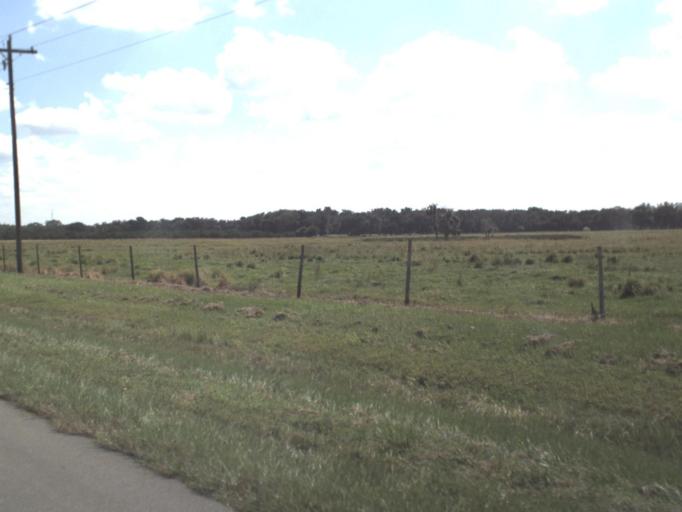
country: US
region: Florida
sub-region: Hardee County
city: Zolfo Springs
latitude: 27.4609
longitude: -81.6933
